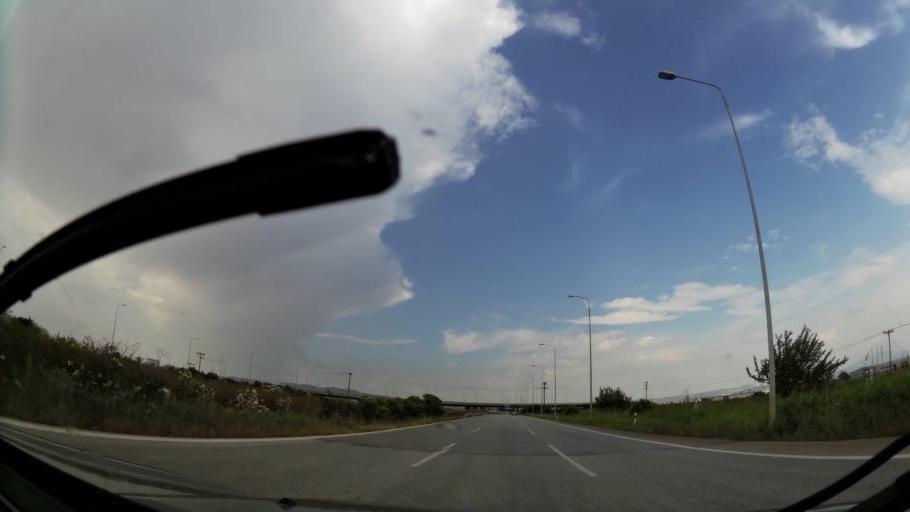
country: GR
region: Central Macedonia
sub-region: Nomos Thessalonikis
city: Sindos
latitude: 40.6478
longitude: 22.8097
